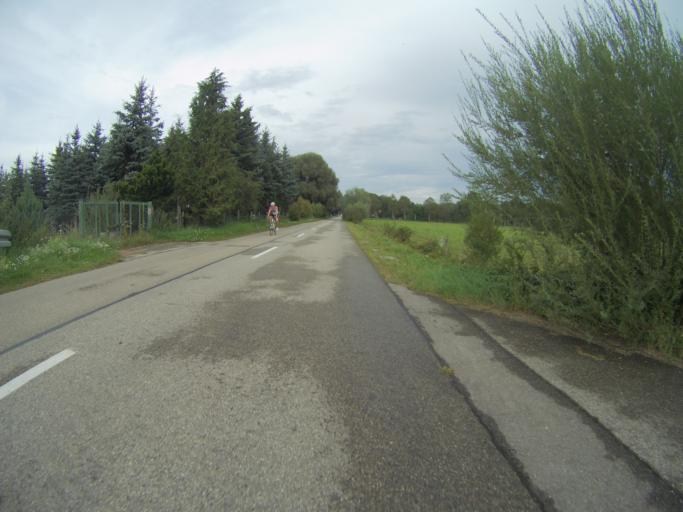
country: DE
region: Bavaria
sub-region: Upper Bavaria
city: Marzling
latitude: 48.3860
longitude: 11.8295
